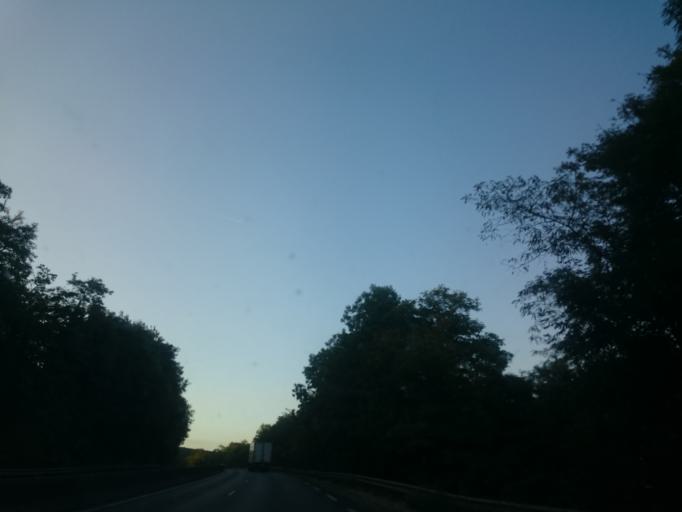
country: FR
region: Ile-de-France
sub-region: Departement de l'Essonne
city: Etrechy
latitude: 48.4986
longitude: 2.2016
